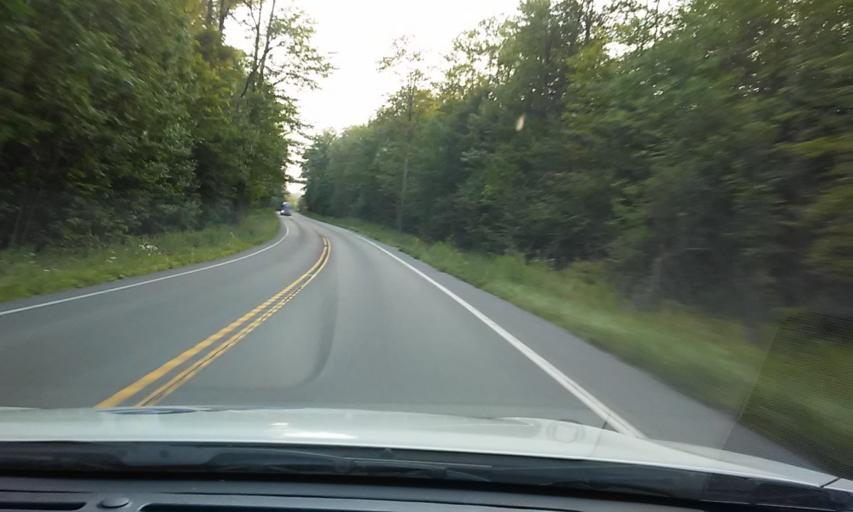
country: US
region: Pennsylvania
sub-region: McKean County
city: Kane
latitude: 41.5819
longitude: -78.8649
